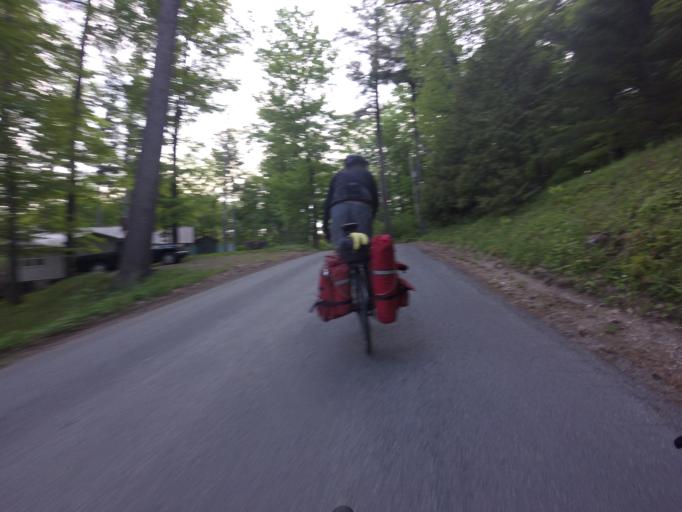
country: US
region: New York
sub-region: St. Lawrence County
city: Gouverneur
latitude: 44.1624
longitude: -75.3820
